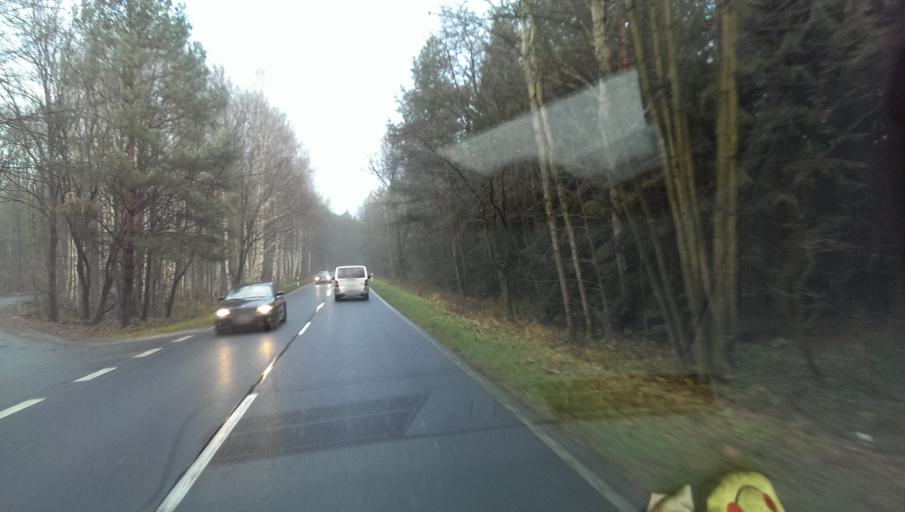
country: DE
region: Saxony
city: Weinbohla
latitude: 51.1826
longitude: 13.6144
